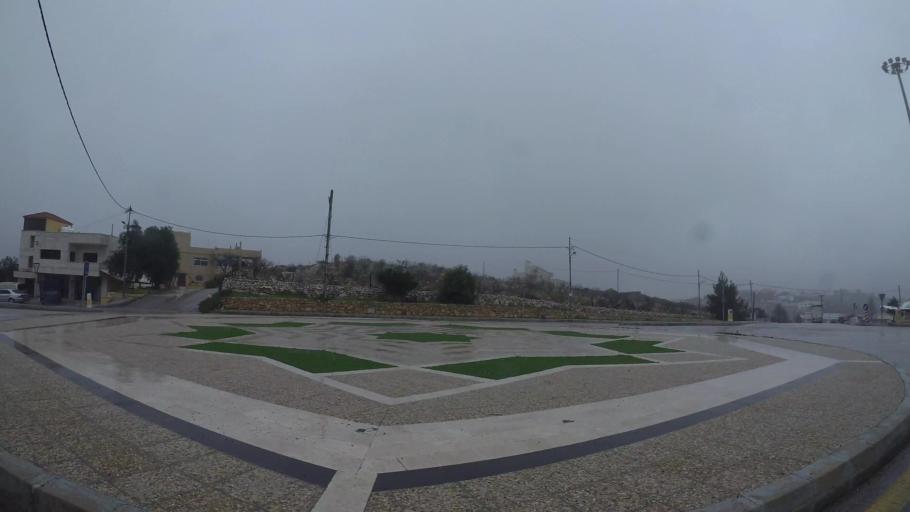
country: JO
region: Amman
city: Wadi as Sir
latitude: 32.0004
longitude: 35.8081
